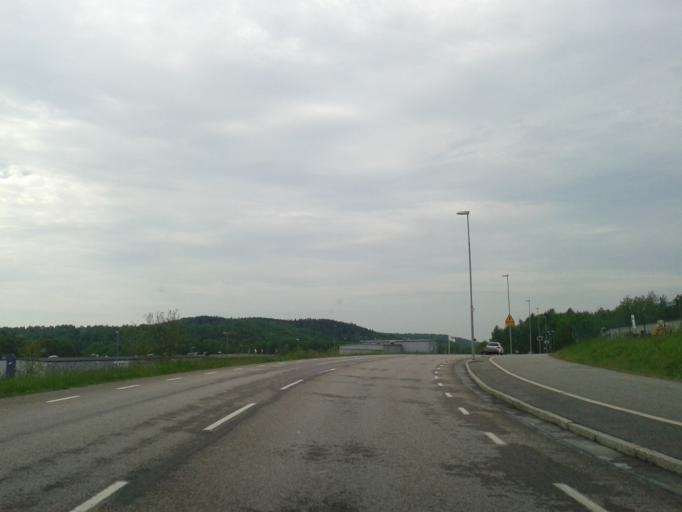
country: SE
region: Vaestra Goetaland
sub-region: Kungalvs Kommun
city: Kungalv
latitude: 57.8765
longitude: 11.9422
